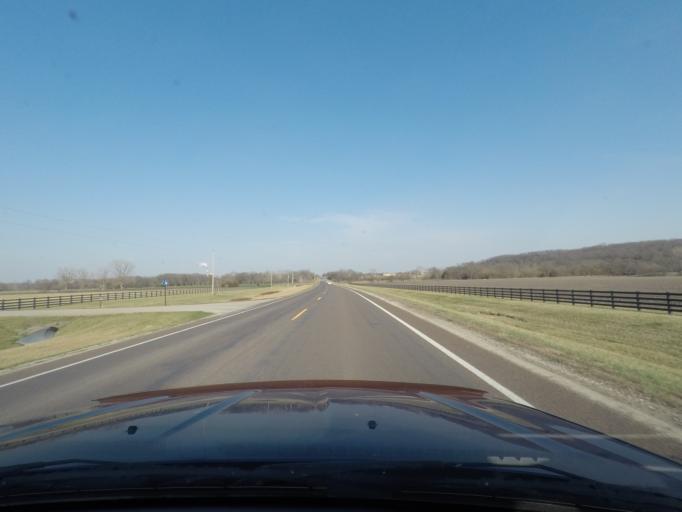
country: US
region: Kansas
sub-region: Douglas County
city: Lawrence
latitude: 39.0007
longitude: -95.3011
